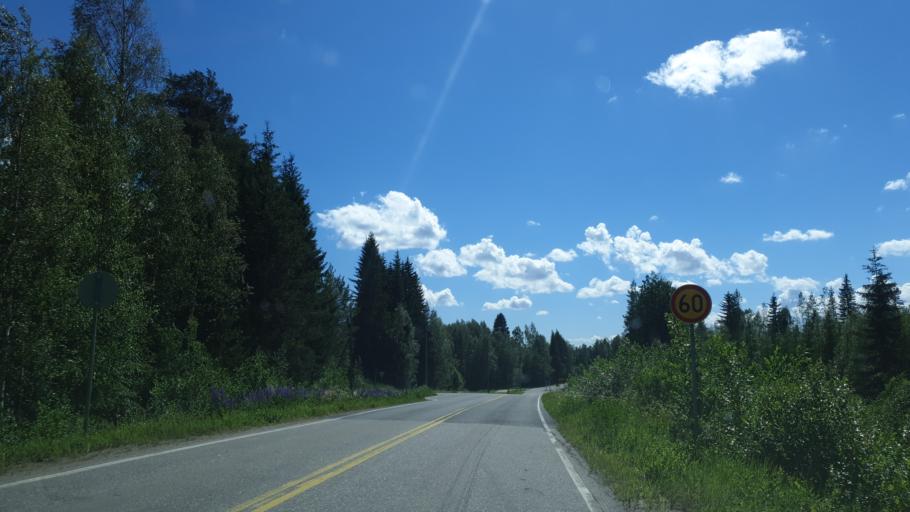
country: FI
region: Northern Savo
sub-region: Koillis-Savo
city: Kaavi
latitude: 62.9881
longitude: 28.5046
